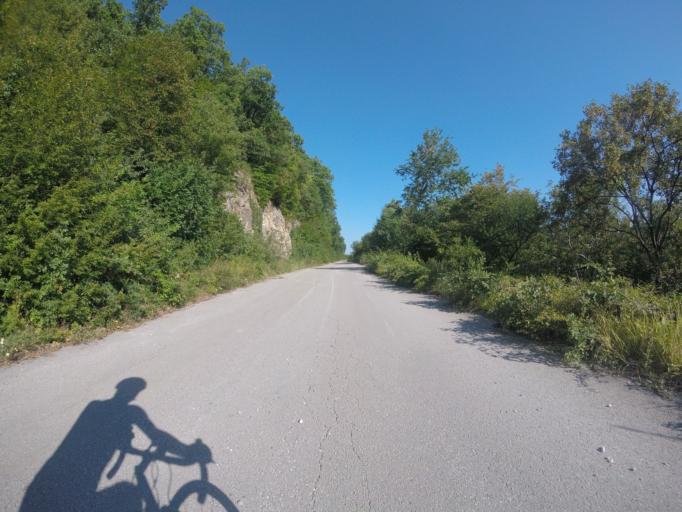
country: HR
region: Primorsko-Goranska
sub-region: Grad Crikvenica
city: Jadranovo
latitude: 45.2592
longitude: 14.6183
